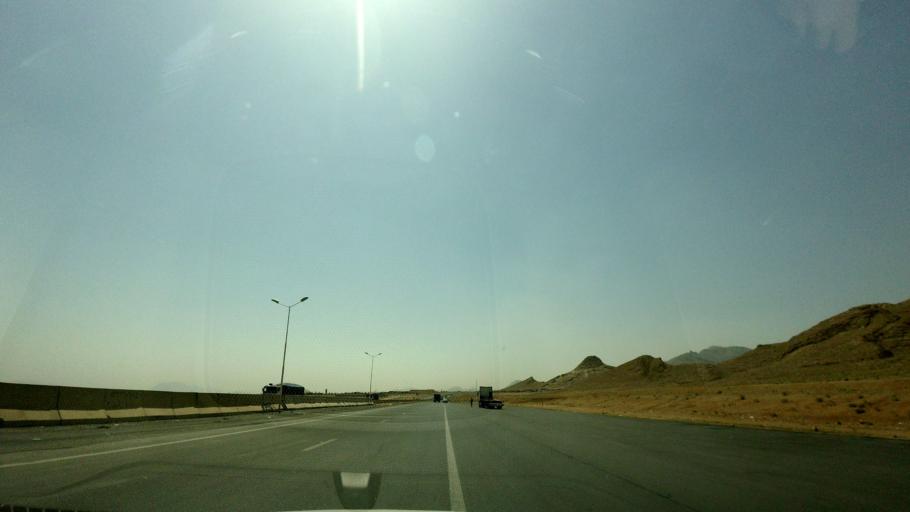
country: IR
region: Isfahan
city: Najafabad
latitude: 32.5811
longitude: 51.2894
